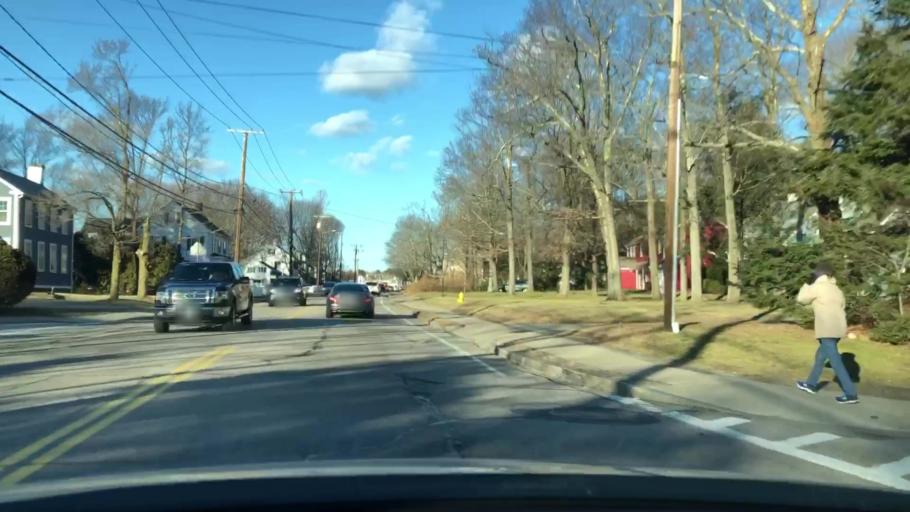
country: US
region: Massachusetts
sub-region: Norfolk County
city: Westwood
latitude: 42.2210
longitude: -71.2234
